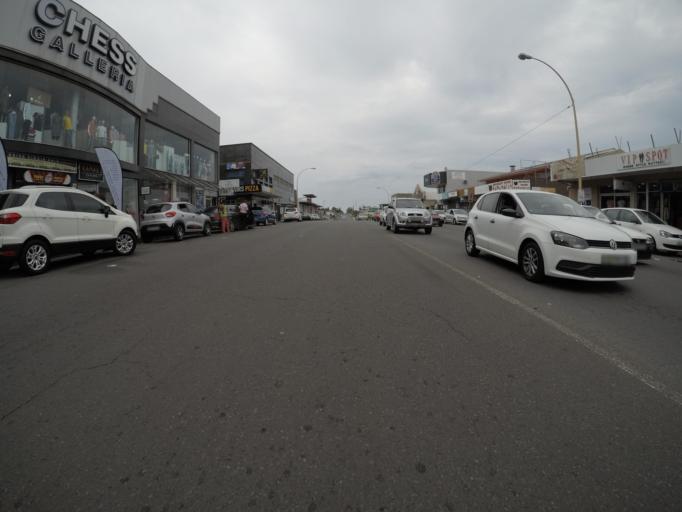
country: ZA
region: Eastern Cape
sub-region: Buffalo City Metropolitan Municipality
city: East London
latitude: -32.9844
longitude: 27.9025
